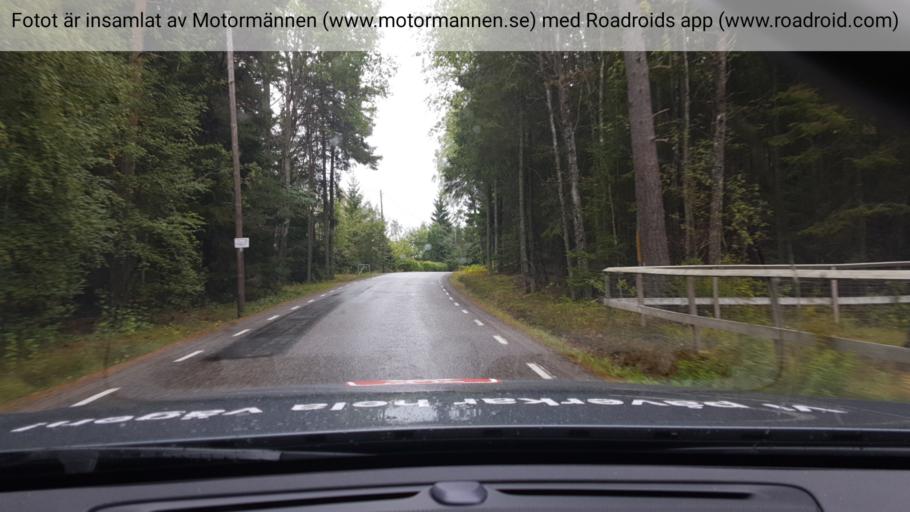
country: SE
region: Stockholm
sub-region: Nynashamns Kommun
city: Osmo
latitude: 59.0472
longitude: 17.8739
